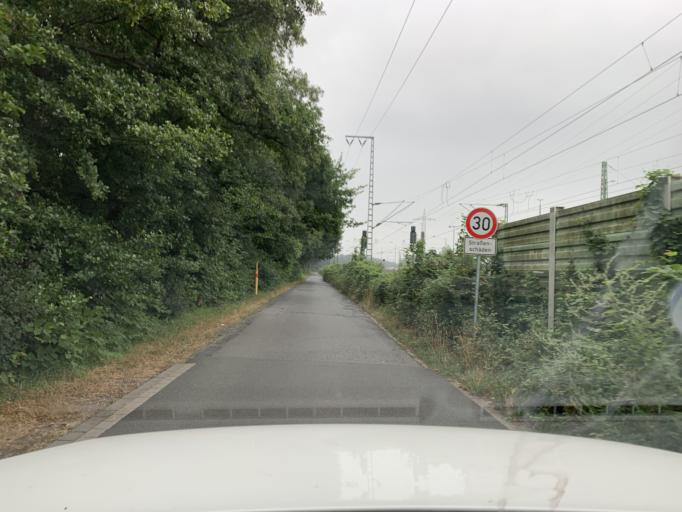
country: DE
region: North Rhine-Westphalia
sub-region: Regierungsbezirk Dusseldorf
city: Duisburg
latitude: 51.3854
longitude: 6.8115
